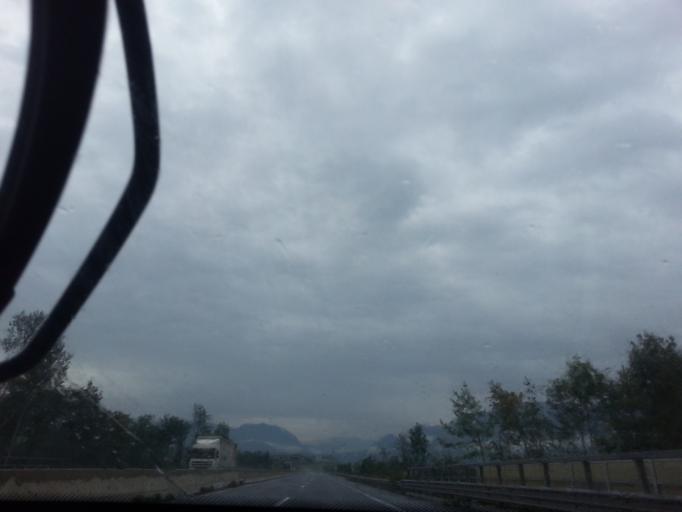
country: AT
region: Upper Austria
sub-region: Politischer Bezirk Kirchdorf an der Krems
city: Micheldorf in Oberoesterreich
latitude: 47.9316
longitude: 14.0966
